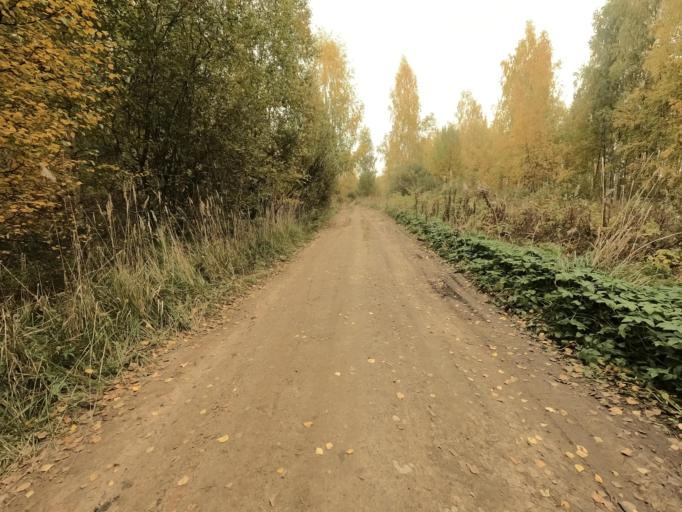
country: RU
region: Novgorod
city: Pankovka
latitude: 58.8655
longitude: 30.9288
